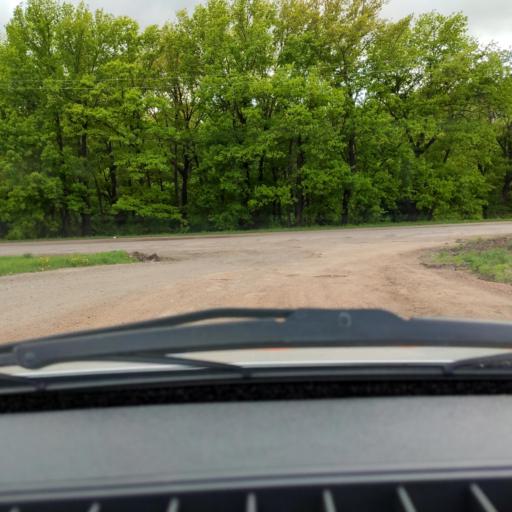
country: RU
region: Bashkortostan
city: Tolbazy
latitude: 54.0043
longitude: 55.8977
